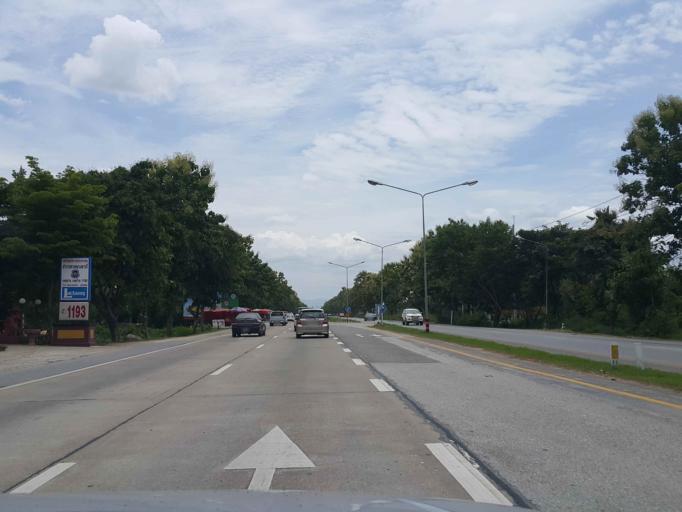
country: TH
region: Chiang Mai
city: Saraphi
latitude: 18.6895
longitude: 99.0499
